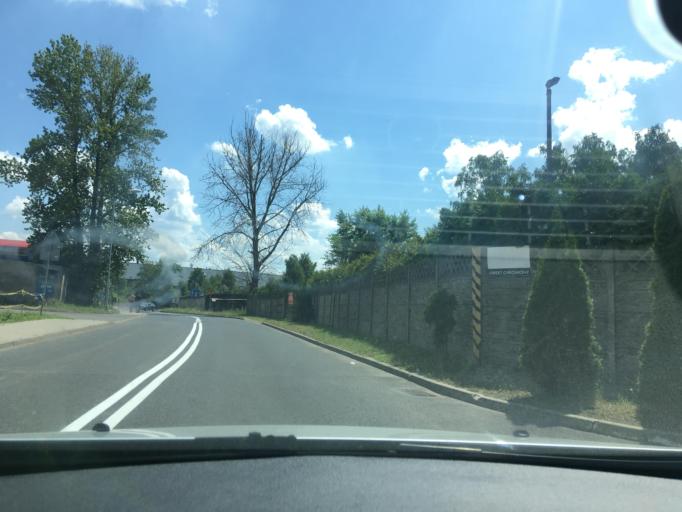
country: PL
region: Silesian Voivodeship
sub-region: Swietochlowice
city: Swietochlowice
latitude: 50.2685
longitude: 18.9477
